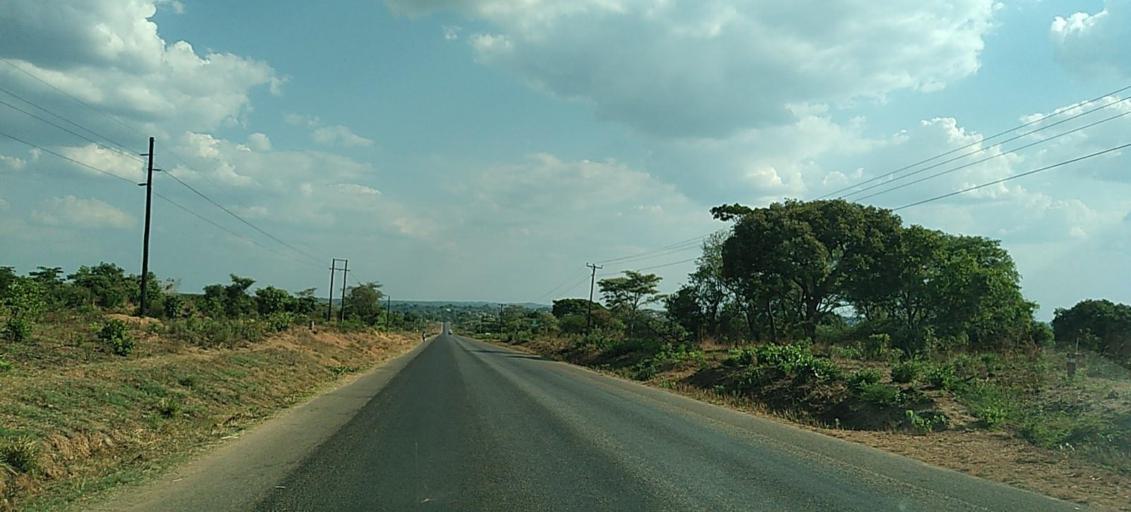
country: ZM
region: Copperbelt
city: Luanshya
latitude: -13.3282
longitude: 28.4159
